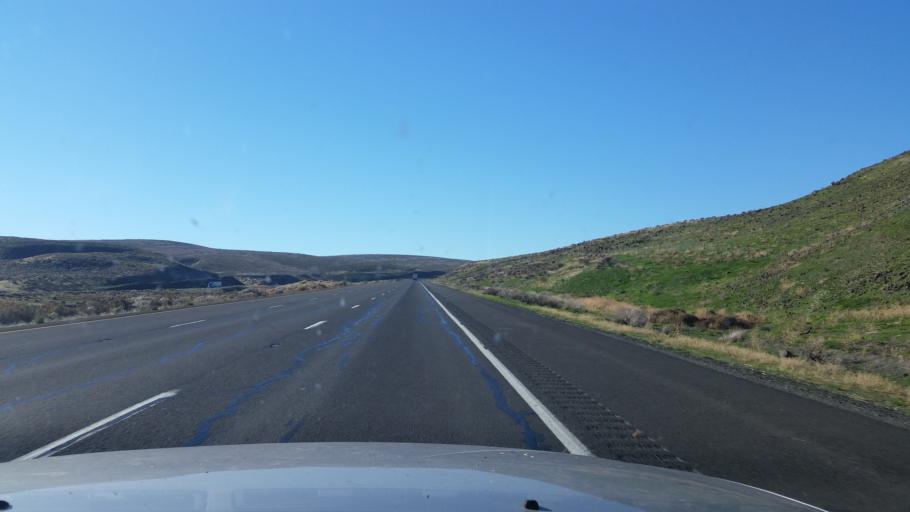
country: US
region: Washington
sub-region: Grant County
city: Mattawa
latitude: 46.9386
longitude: -120.0339
